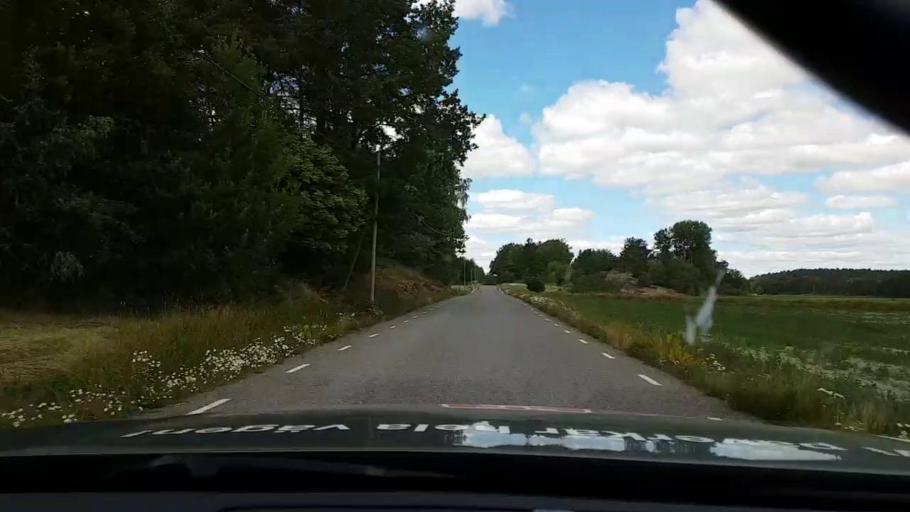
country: SE
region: Kalmar
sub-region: Vasterviks Kommun
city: Forserum
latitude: 57.9924
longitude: 16.6018
